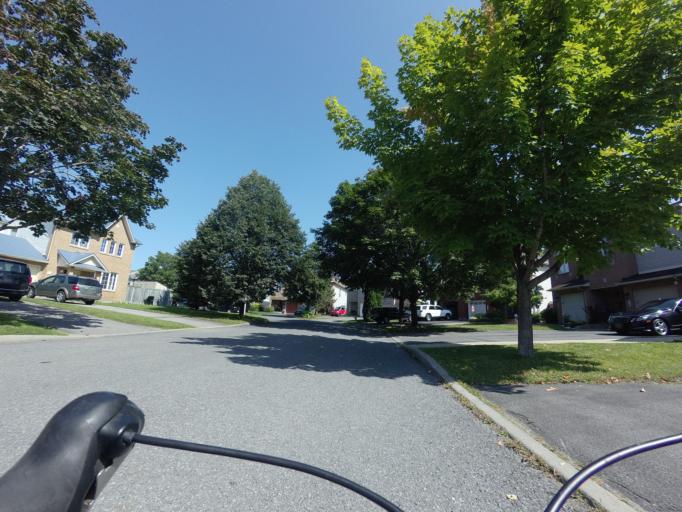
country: CA
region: Ontario
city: Bells Corners
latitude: 45.2781
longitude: -75.8535
